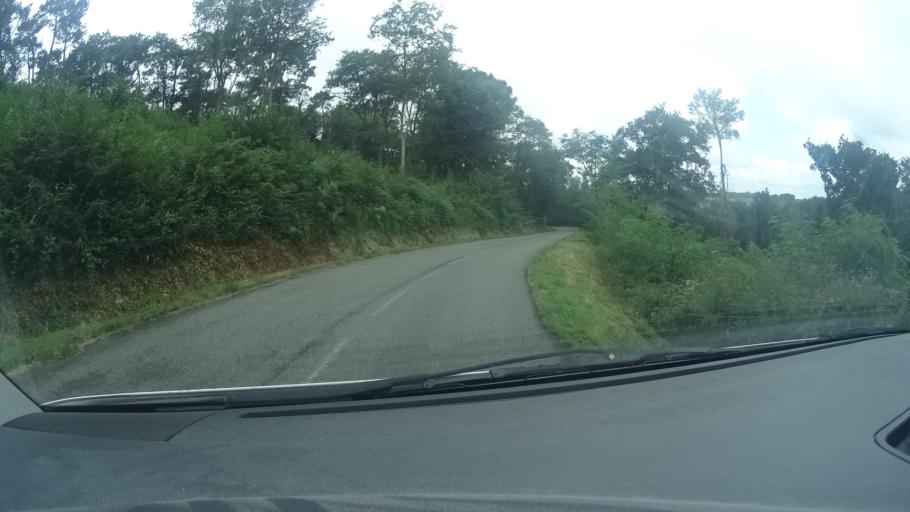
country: FR
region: Aquitaine
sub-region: Departement des Pyrenees-Atlantiques
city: Mont
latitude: 43.4870
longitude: -0.6870
